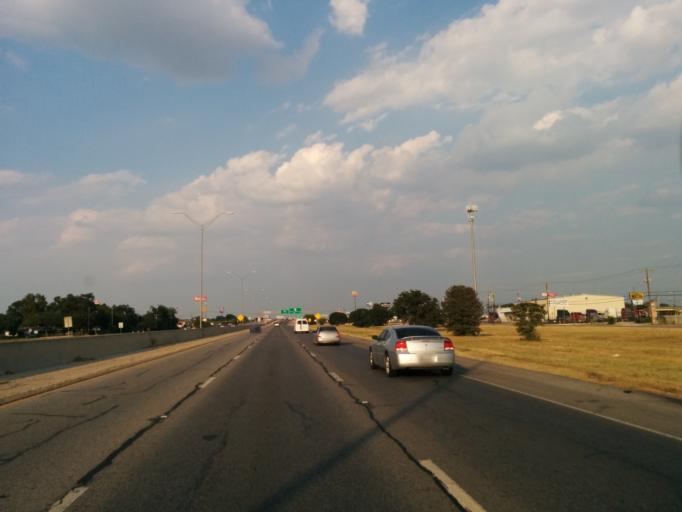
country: US
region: Texas
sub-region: Bexar County
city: Kirby
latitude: 29.4298
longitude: -98.4123
